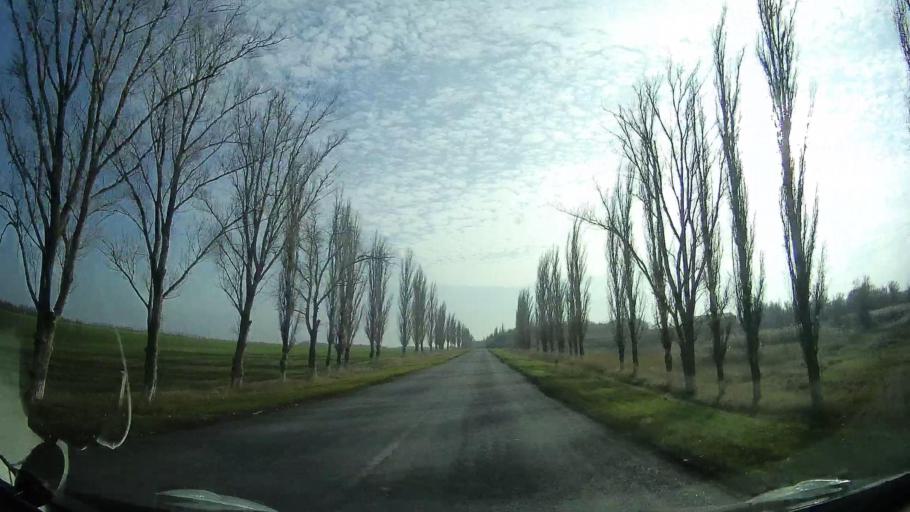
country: RU
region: Rostov
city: Mechetinskaya
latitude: 46.8298
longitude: 40.5516
